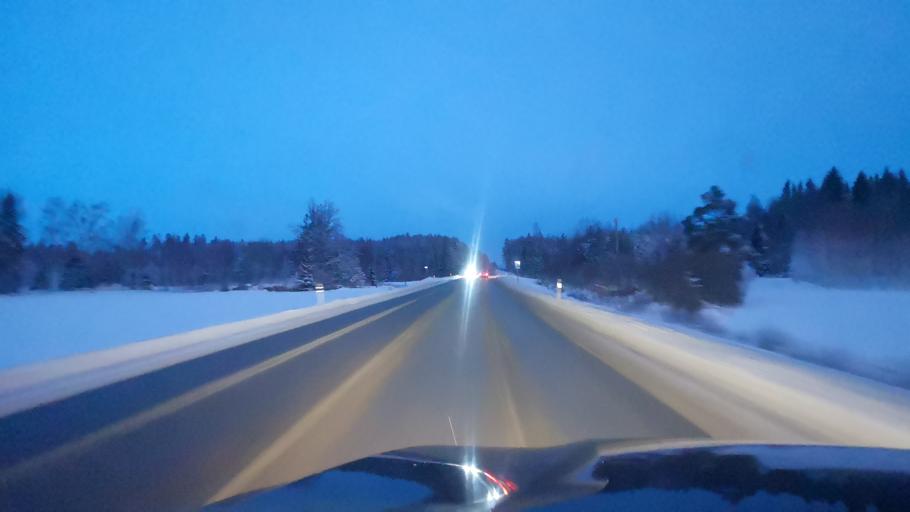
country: FI
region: Varsinais-Suomi
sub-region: Loimaa
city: Loimaa
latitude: 60.8662
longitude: 23.0541
